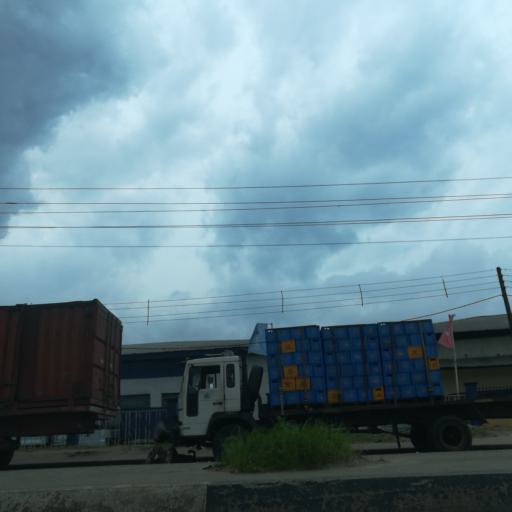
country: NG
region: Rivers
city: Port Harcourt
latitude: 4.8219
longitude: 7.0398
